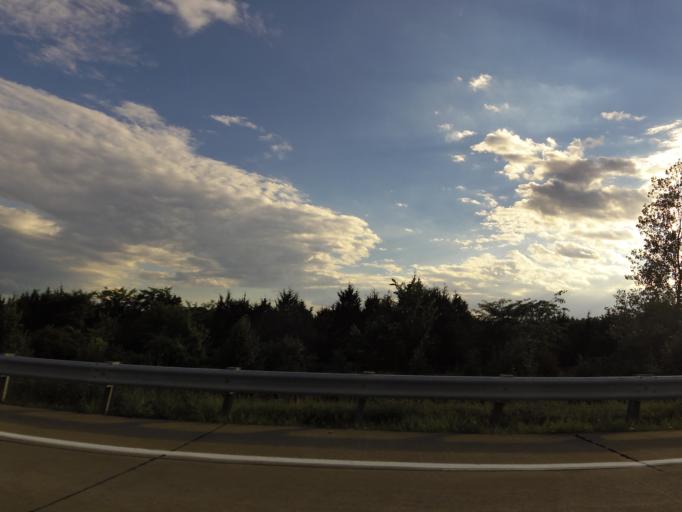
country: US
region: Missouri
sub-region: Saint Charles County
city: Dardenne Prairie
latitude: 38.7521
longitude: -90.7565
